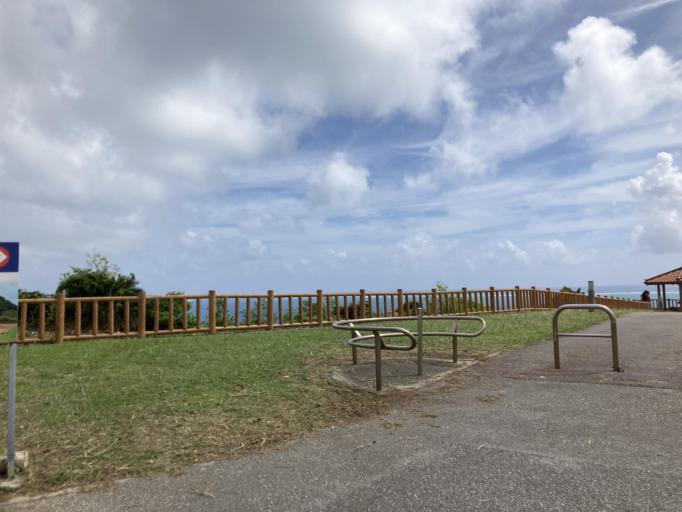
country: JP
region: Okinawa
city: Ginowan
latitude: 26.1679
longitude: 127.8291
